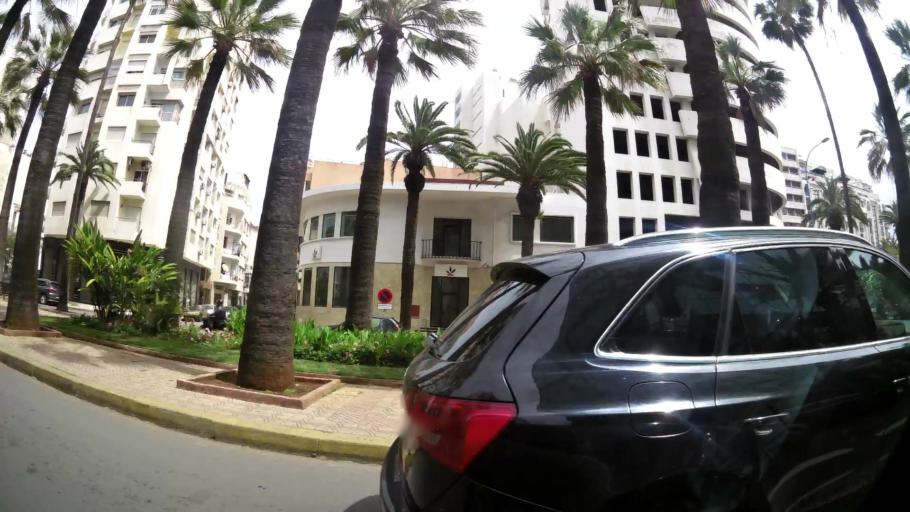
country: MA
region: Grand Casablanca
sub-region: Casablanca
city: Casablanca
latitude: 33.5945
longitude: -7.6296
